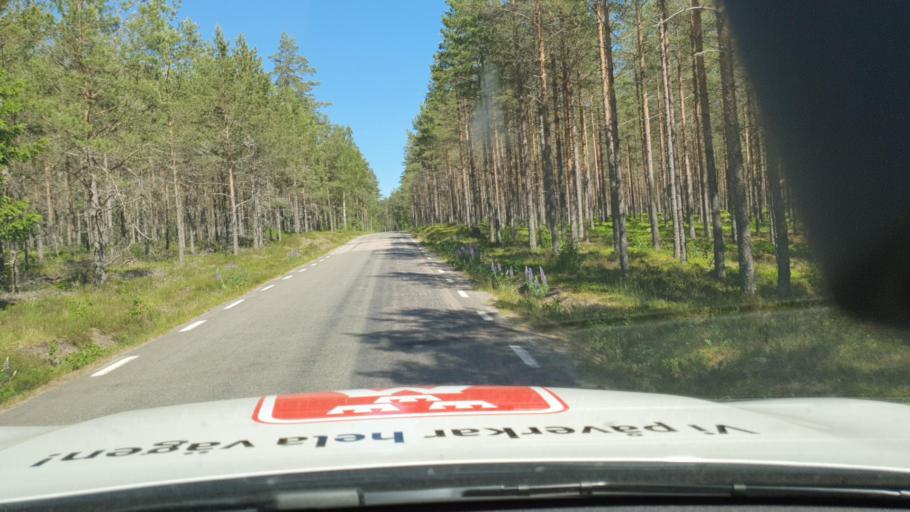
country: SE
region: Joenkoeping
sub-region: Habo Kommun
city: Habo
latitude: 58.0490
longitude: 14.0276
